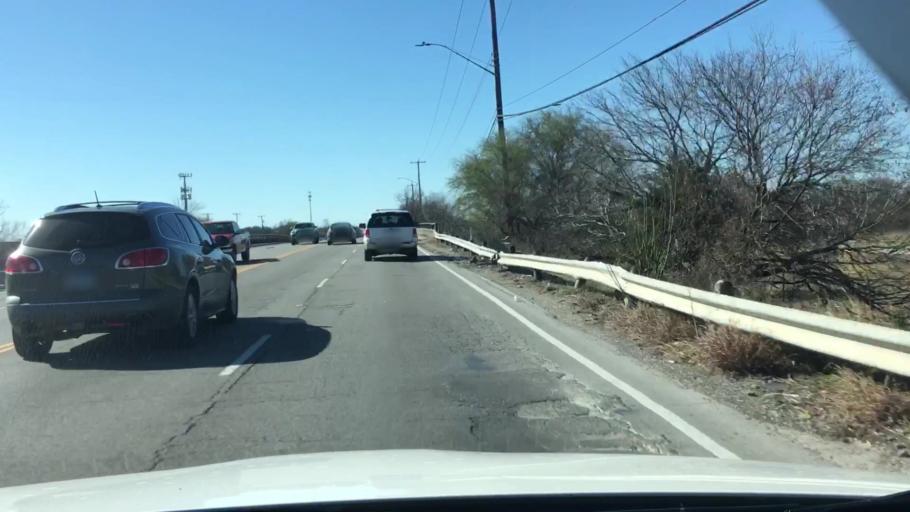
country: US
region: Texas
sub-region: Bexar County
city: Alamo Heights
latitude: 29.5428
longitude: -98.4412
